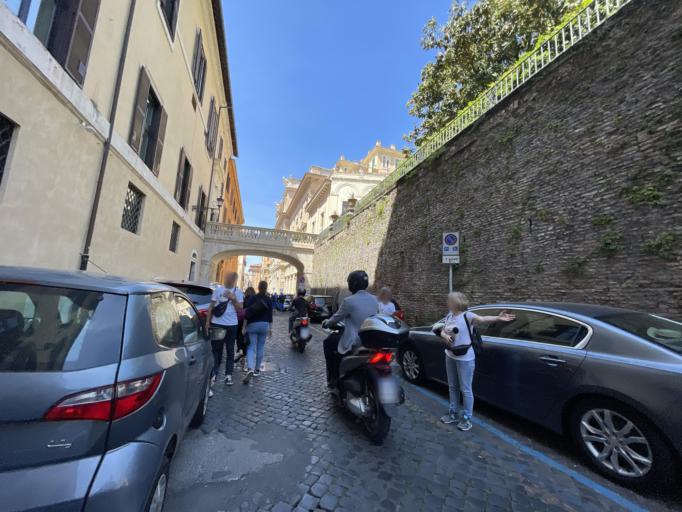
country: IT
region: Latium
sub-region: Citta metropolitana di Roma Capitale
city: Rome
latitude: 41.8982
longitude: 12.4846
